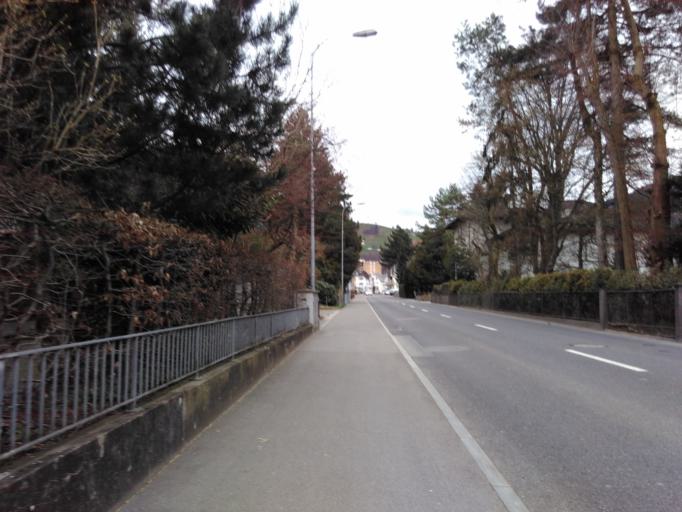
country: CH
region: Schwyz
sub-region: Bezirk March
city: Schubelbach
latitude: 47.1805
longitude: 8.8978
